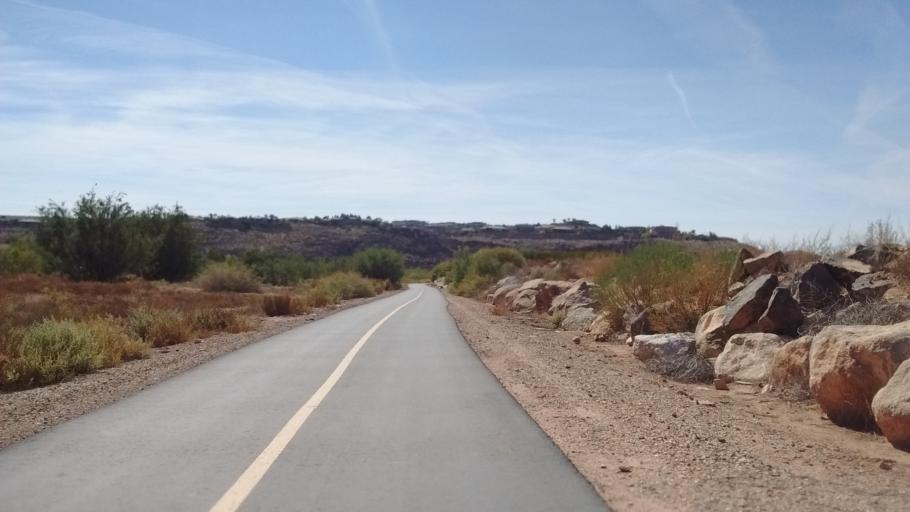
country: US
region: Utah
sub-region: Washington County
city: Saint George
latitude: 37.0909
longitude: -113.5378
